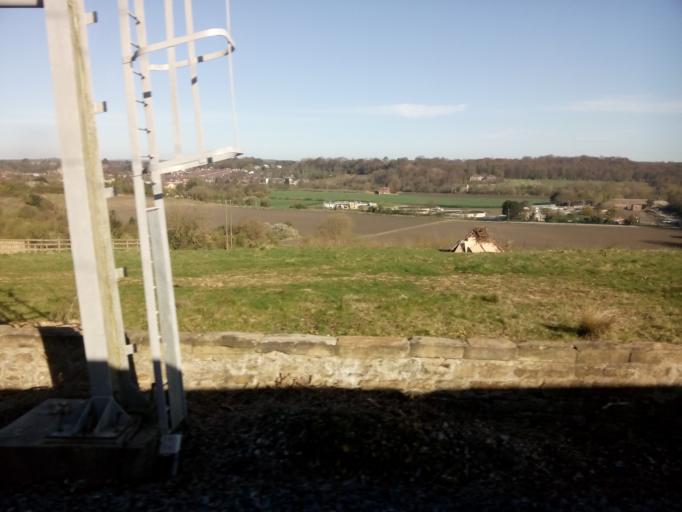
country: GB
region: England
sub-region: Northumberland
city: Morpeth
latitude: 55.1649
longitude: -1.6733
